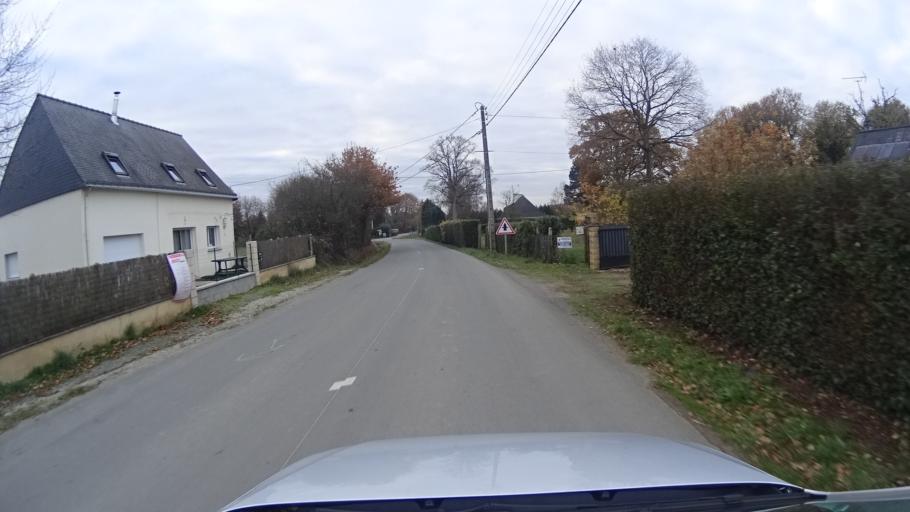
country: FR
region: Brittany
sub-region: Departement d'Ille-et-Vilaine
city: Sainte-Marie
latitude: 47.6937
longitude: -1.9341
